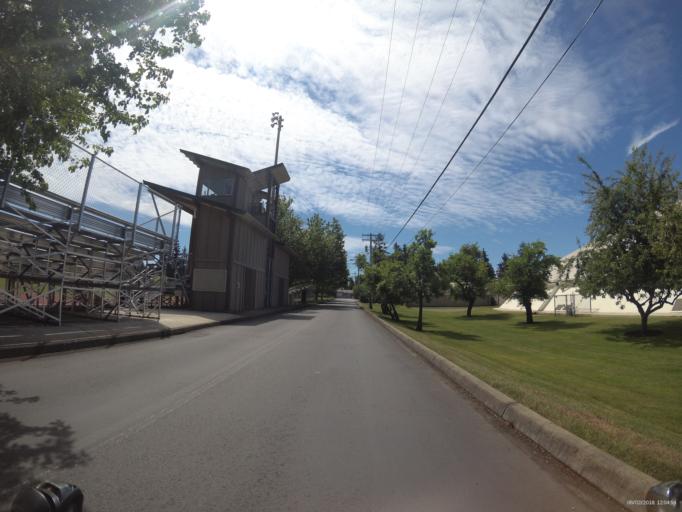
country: US
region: Washington
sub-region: Pierce County
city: University Place
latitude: 47.2003
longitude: -122.5458
